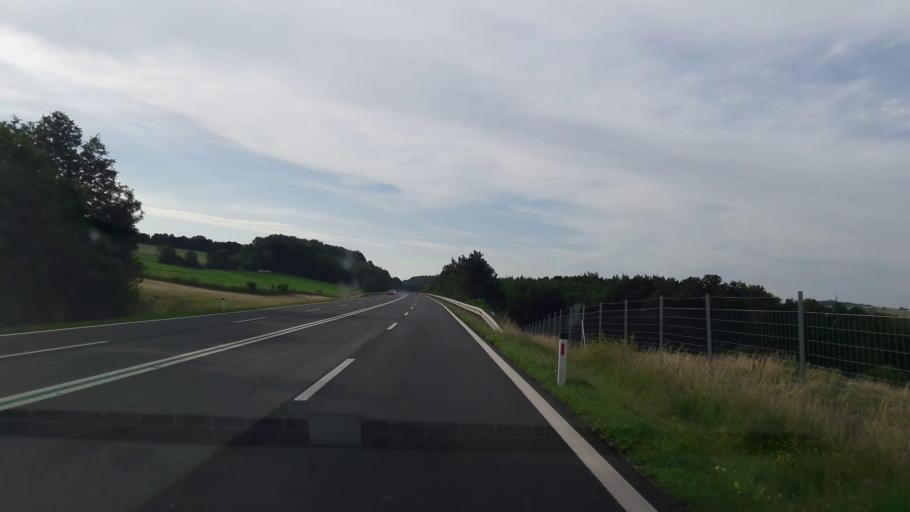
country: AT
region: Burgenland
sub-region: Politischer Bezirk Oberpullendorf
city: Kobersdorf
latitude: 47.6225
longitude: 16.3875
